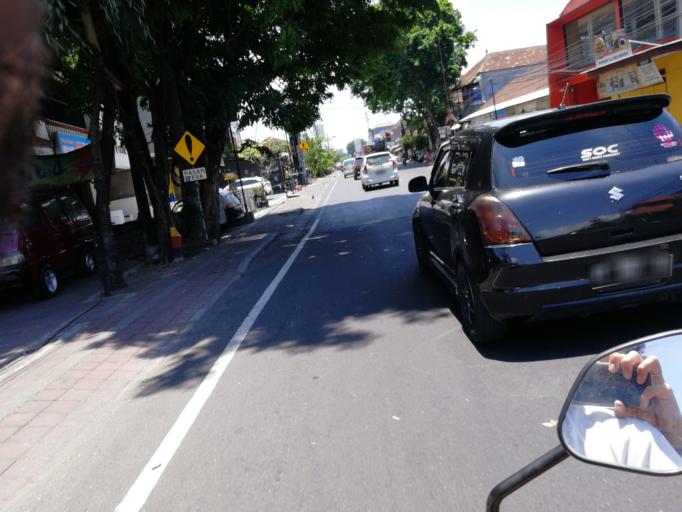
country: ID
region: Bali
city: Karyadharma
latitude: -8.6878
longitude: 115.1924
